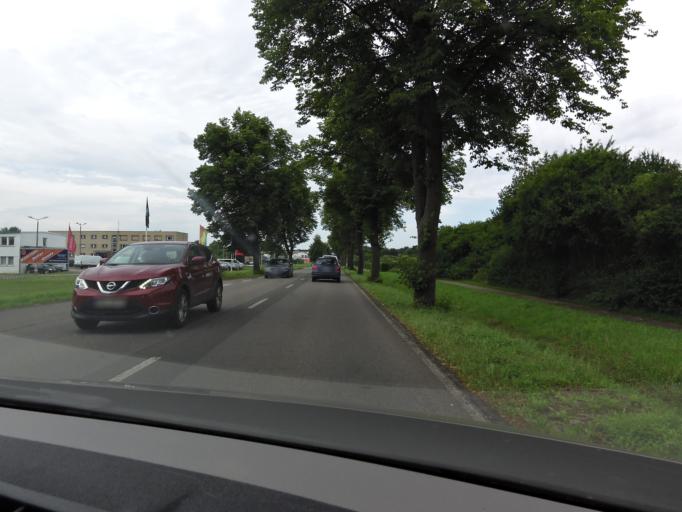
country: DE
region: Mecklenburg-Vorpommern
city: Neustrelitz
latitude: 53.3448
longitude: 13.0918
